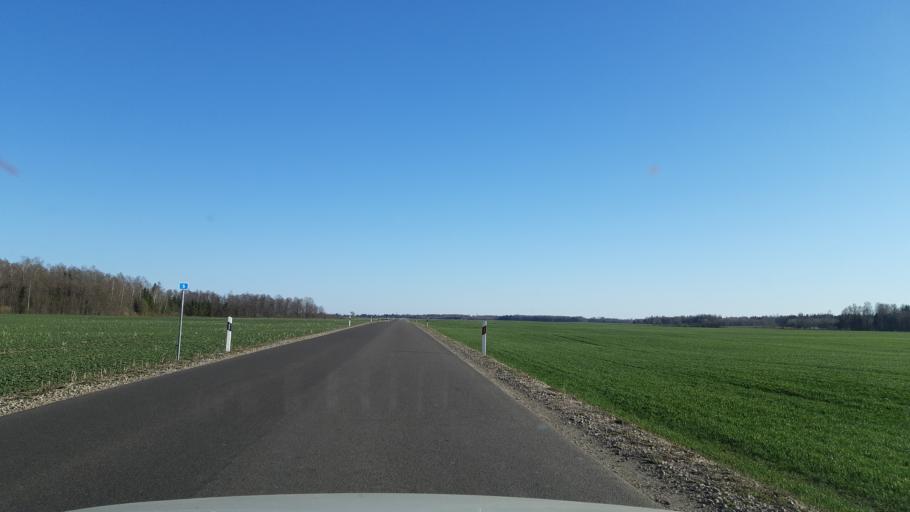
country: LT
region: Kauno apskritis
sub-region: Kaunas
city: Sargenai
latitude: 55.0276
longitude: 23.7604
